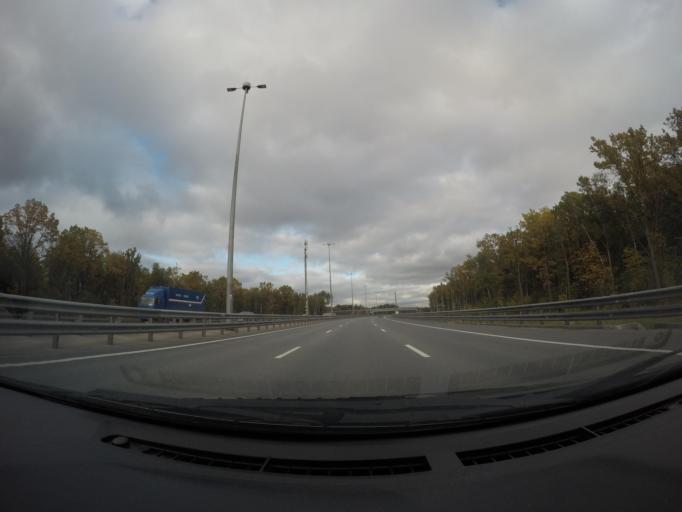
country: RU
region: Moskovskaya
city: Lesnoy Gorodok
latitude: 55.6753
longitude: 37.2265
